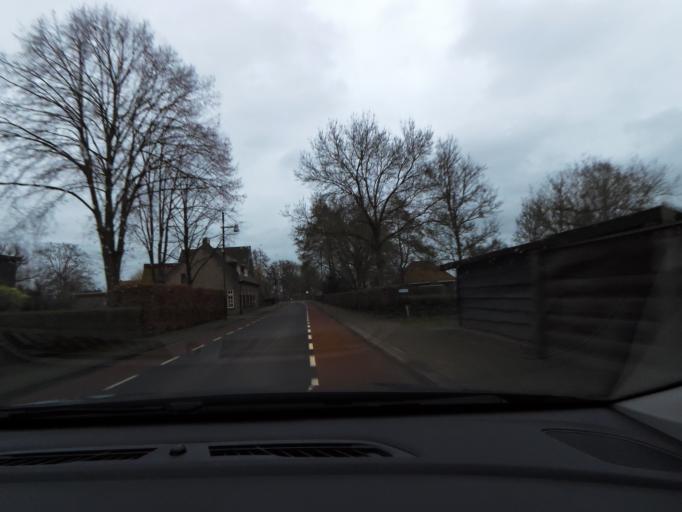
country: NL
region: North Brabant
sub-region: Gemeente Waalwijk
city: Waspik
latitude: 51.6894
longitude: 4.9841
